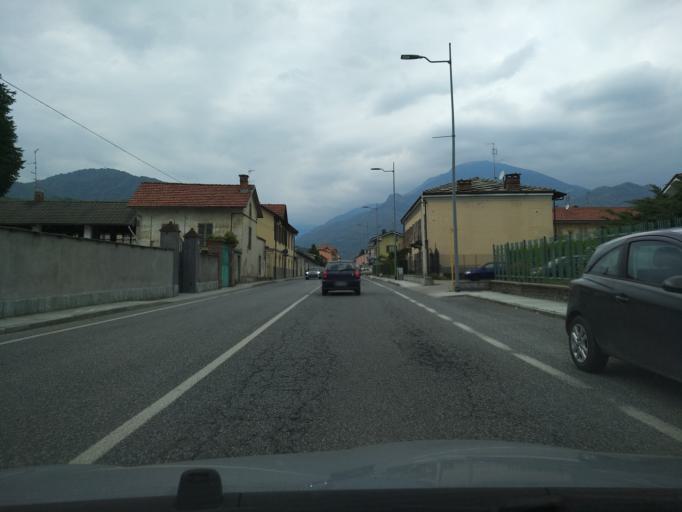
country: IT
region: Piedmont
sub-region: Provincia di Torino
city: Airali
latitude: 44.8129
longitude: 7.2549
